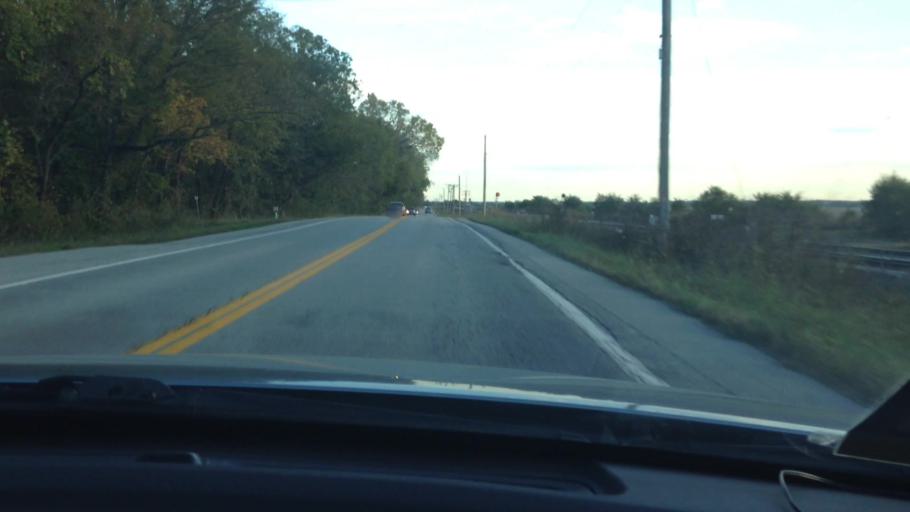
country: US
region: Kansas
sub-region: Leavenworth County
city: Lansing
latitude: 39.3003
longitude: -94.8461
